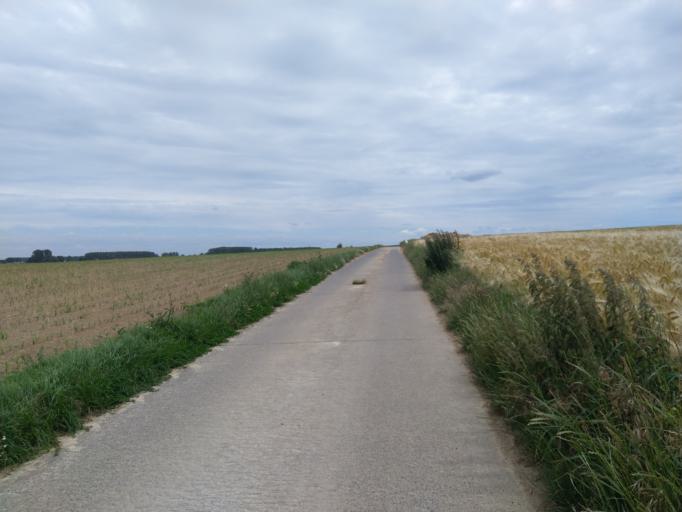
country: BE
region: Wallonia
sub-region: Province du Hainaut
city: Beloeil
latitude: 50.5418
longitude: 3.7816
